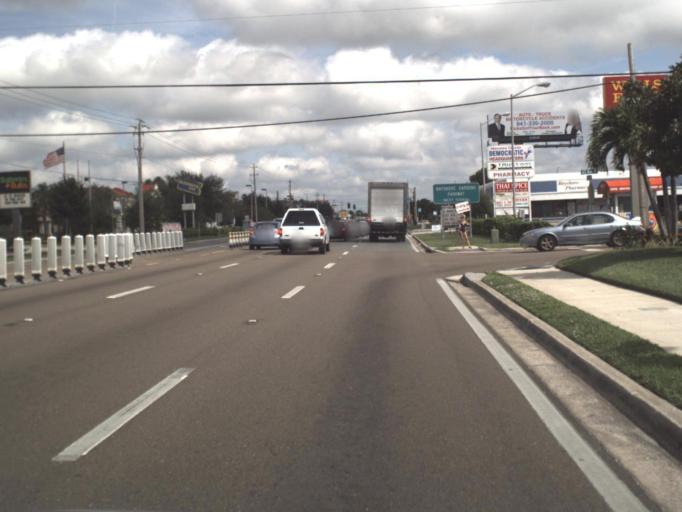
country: US
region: Florida
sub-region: Manatee County
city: Bayshore Gardens
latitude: 27.4290
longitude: -82.5754
